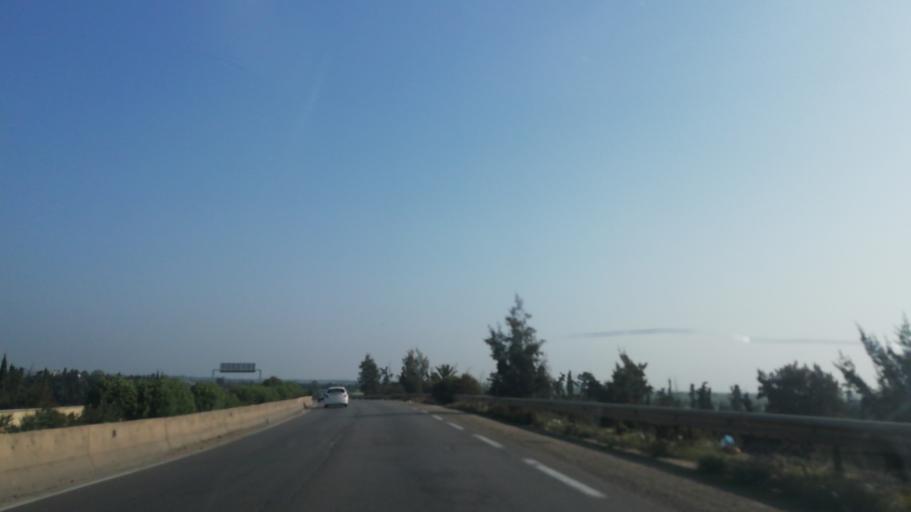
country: DZ
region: Oran
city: Bou Tlelis
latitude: 35.5659
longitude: -0.9041
